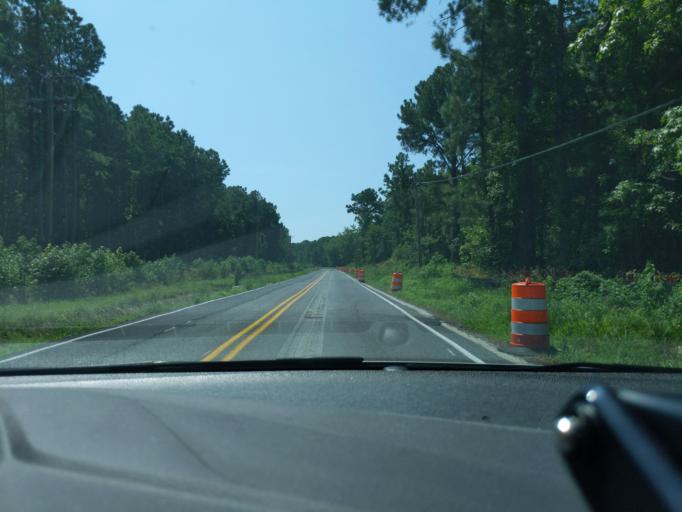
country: US
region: Virginia
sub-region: Northumberland County
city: Heathsville
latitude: 38.0726
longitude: -76.3395
